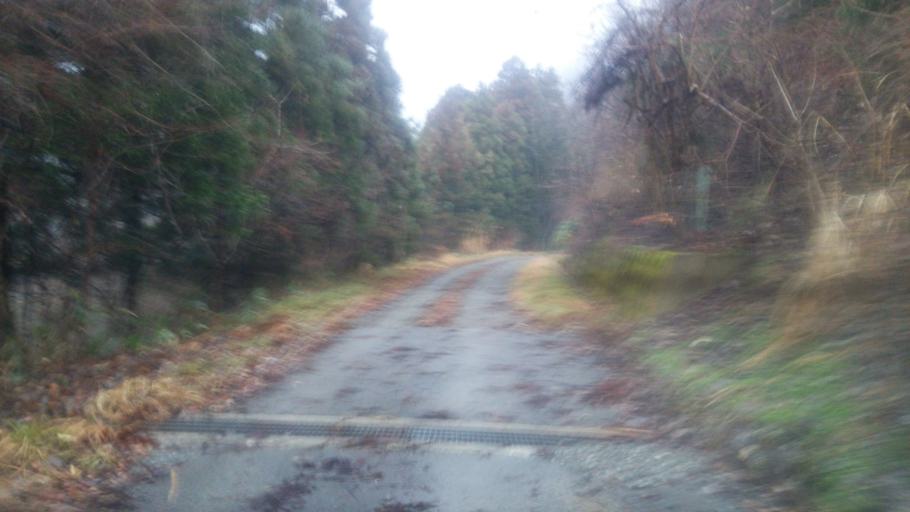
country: JP
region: Fukushima
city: Kitakata
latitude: 37.5787
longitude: 139.9701
